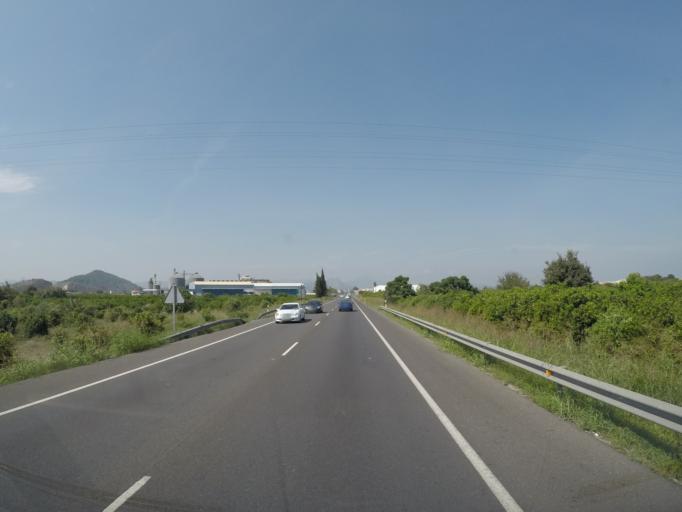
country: ES
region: Valencia
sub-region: Provincia de Valencia
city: Oliva
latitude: 38.9264
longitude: -0.1289
